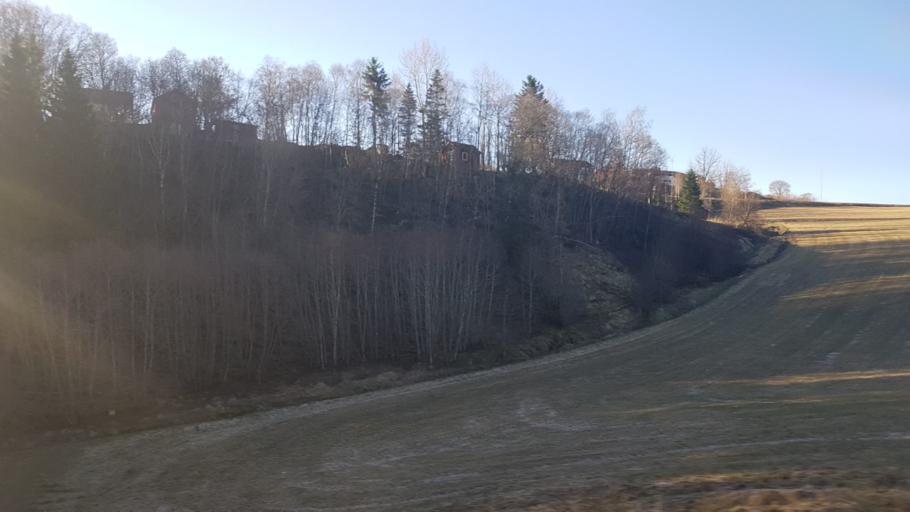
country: NO
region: Nord-Trondelag
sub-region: Levanger
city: Skogn
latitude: 63.6741
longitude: 11.1007
